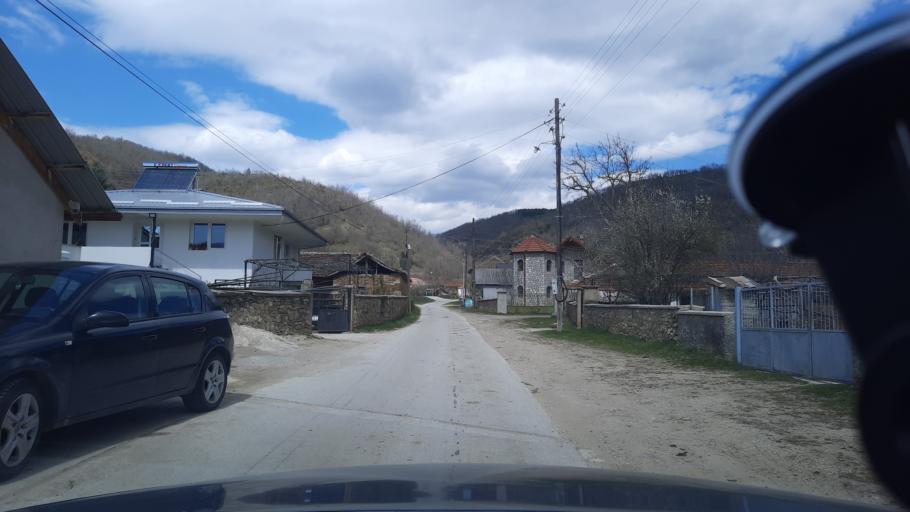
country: MK
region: Demir Hisar
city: Sopotnica
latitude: 41.2978
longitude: 21.1527
